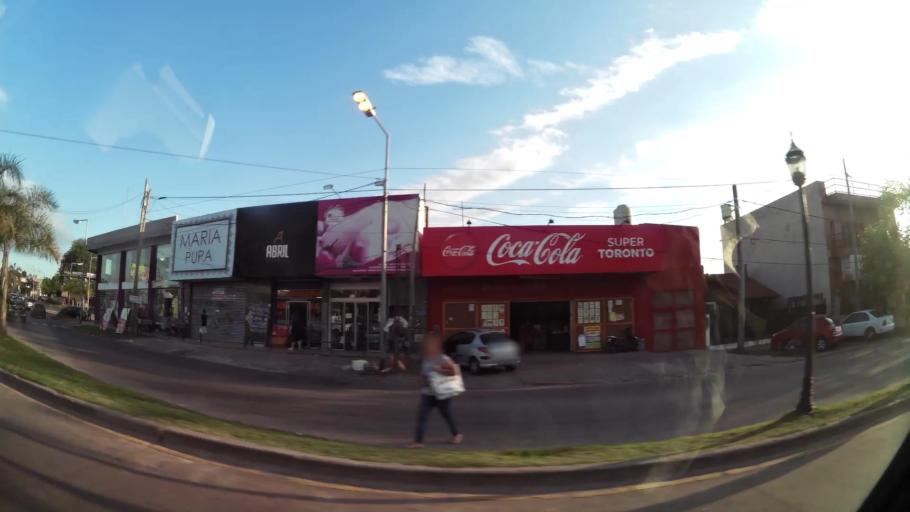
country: AR
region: Buenos Aires
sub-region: Partido de Tigre
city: Tigre
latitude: -34.4536
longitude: -58.6427
